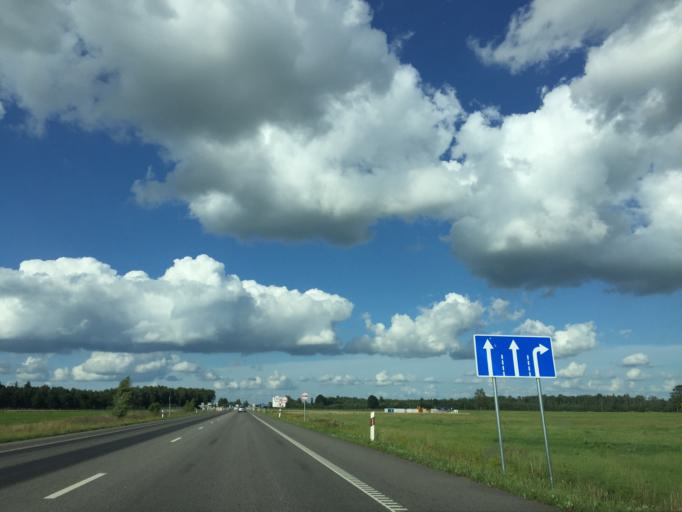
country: LT
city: Kazlu Ruda
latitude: 54.6615
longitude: 23.5085
